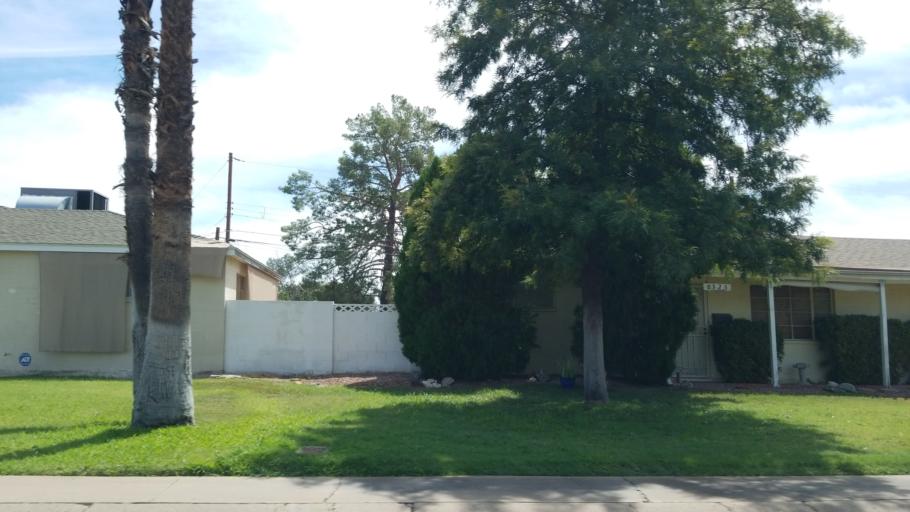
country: US
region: Arizona
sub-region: Maricopa County
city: Glendale
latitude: 33.5596
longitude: -112.1256
